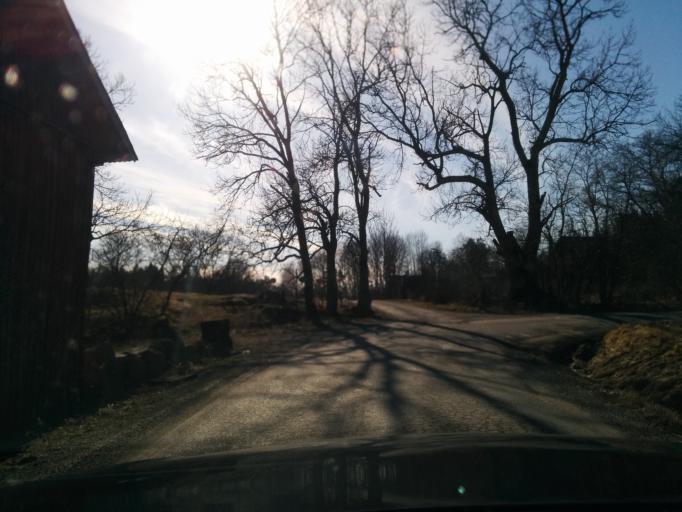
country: SE
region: Stockholm
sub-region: Vallentuna Kommun
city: Vallentuna
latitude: 59.5196
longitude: 18.0311
